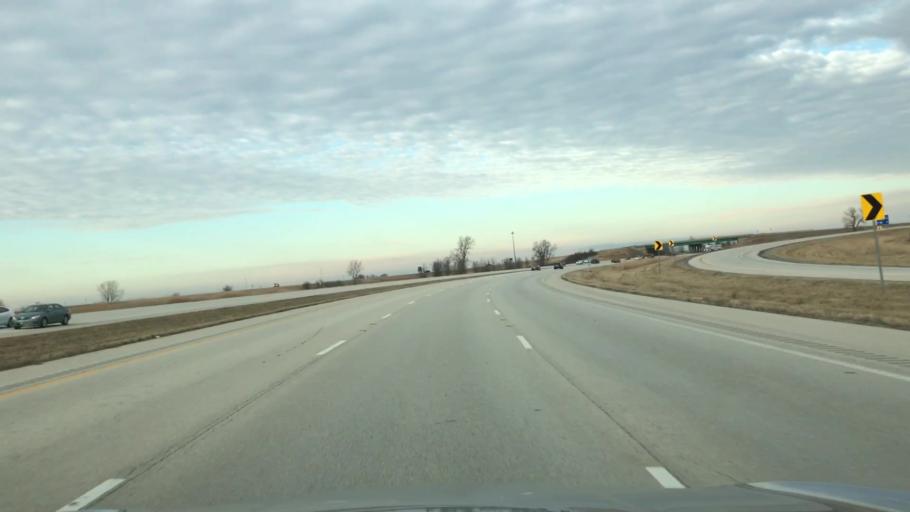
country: US
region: Illinois
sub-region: Sangamon County
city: Williamsville
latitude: 39.9547
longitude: -89.5576
